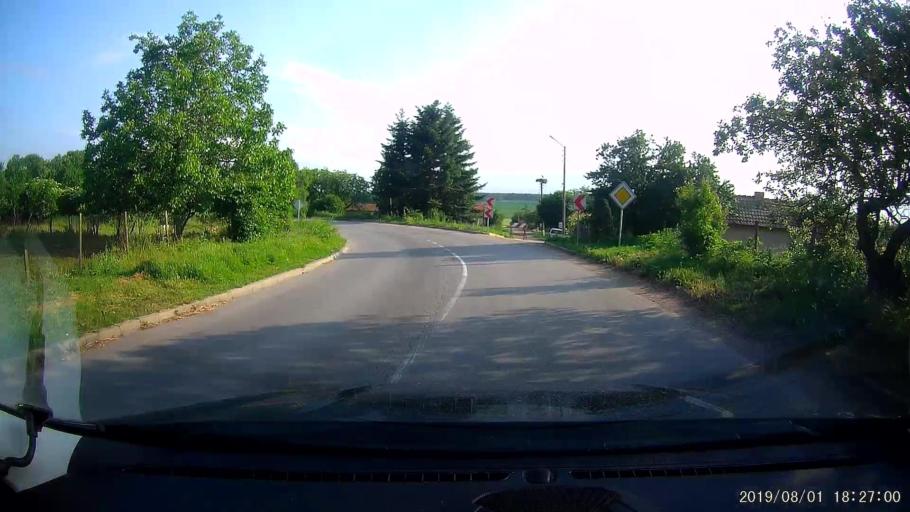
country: BG
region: Shumen
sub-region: Obshtina Venets
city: Venets
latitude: 43.5933
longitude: 26.9830
